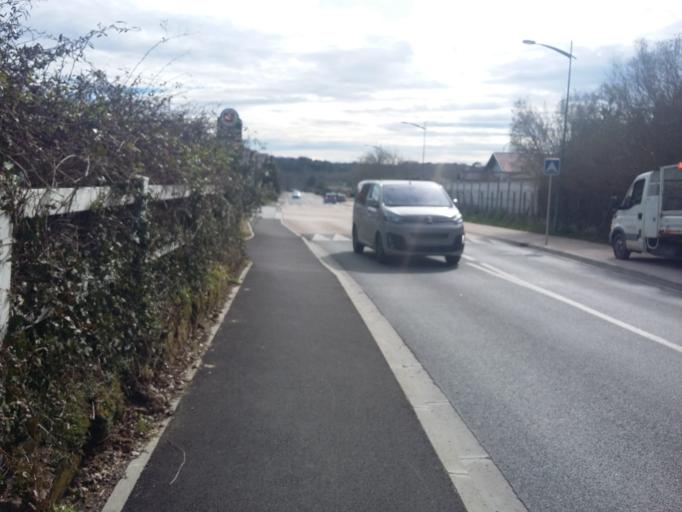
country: FR
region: Aquitaine
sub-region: Departement des Landes
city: Saint-Martin-de-Seignanx
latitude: 43.5429
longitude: -1.3872
